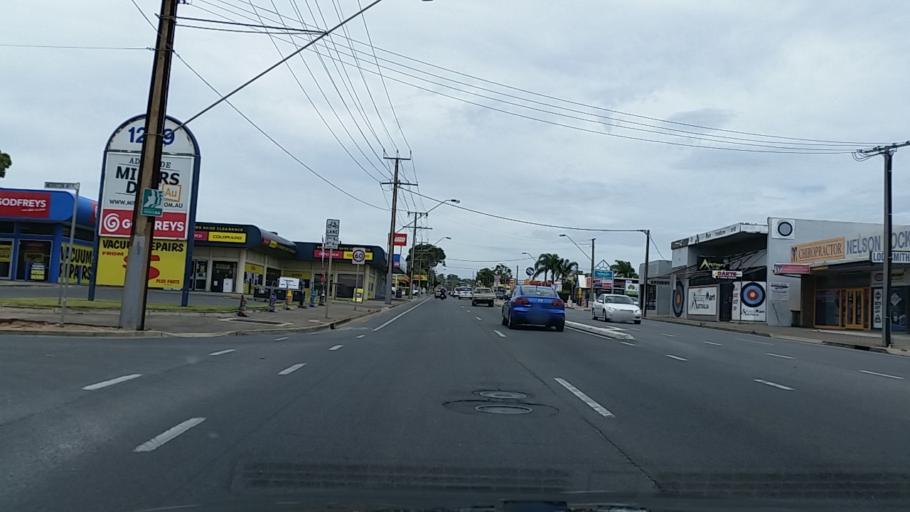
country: AU
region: South Australia
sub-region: Marion
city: Clovelly Park
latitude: -35.0007
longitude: 138.5755
